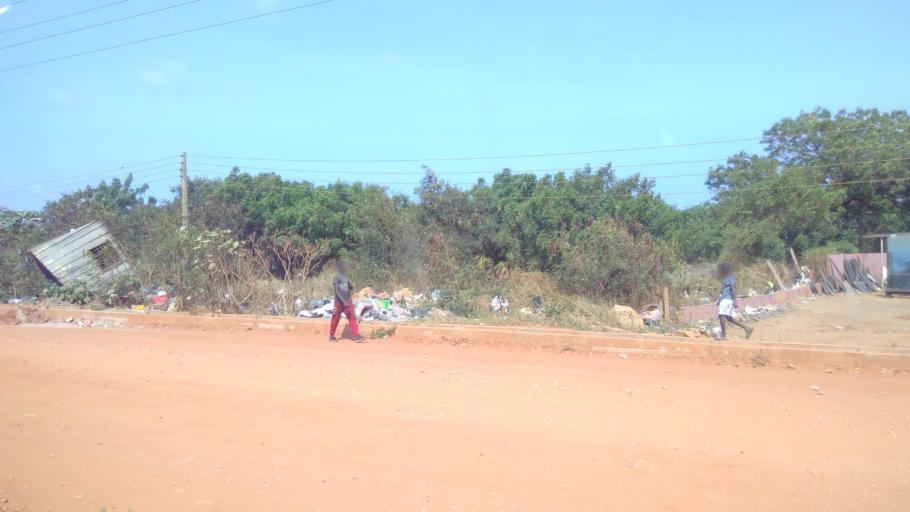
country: GH
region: Greater Accra
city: Nungua
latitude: 5.6312
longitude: -0.0658
